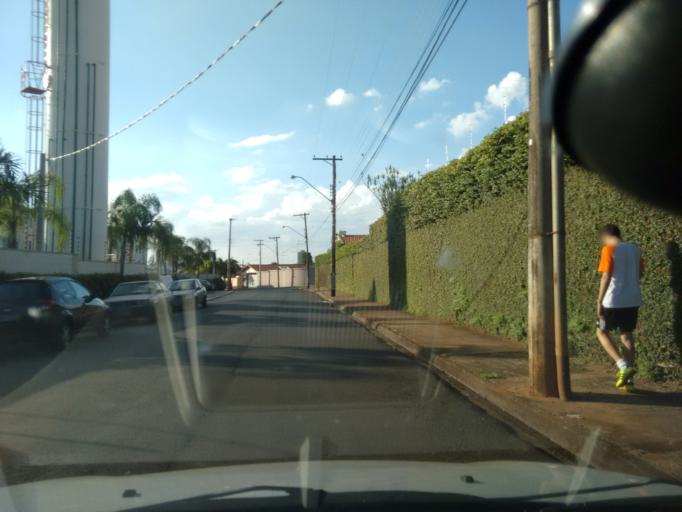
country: BR
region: Sao Paulo
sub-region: Araraquara
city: Araraquara
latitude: -21.7992
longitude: -48.1943
